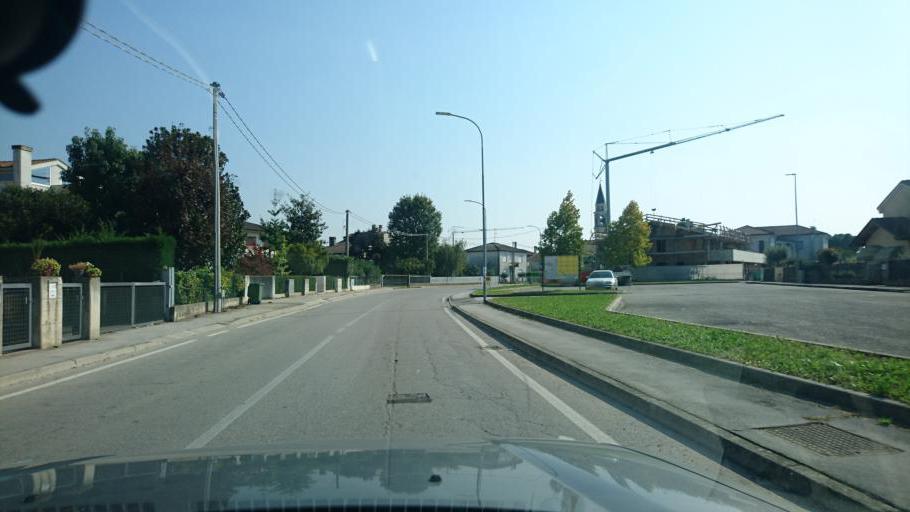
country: IT
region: Veneto
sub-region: Provincia di Padova
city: Campodoro
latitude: 45.5124
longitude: 11.7406
